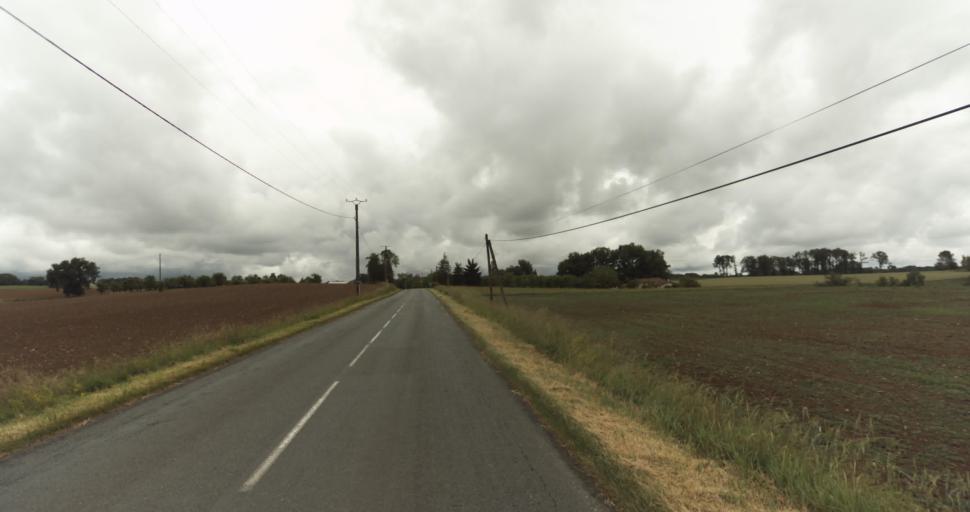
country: FR
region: Aquitaine
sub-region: Departement de la Dordogne
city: Beaumont-du-Perigord
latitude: 44.7201
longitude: 0.7952
